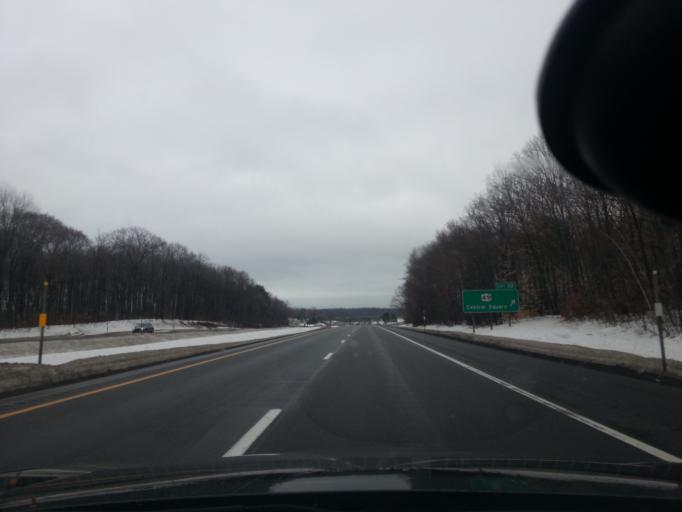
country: US
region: New York
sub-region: Oswego County
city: Central Square
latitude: 43.2920
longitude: -76.1251
